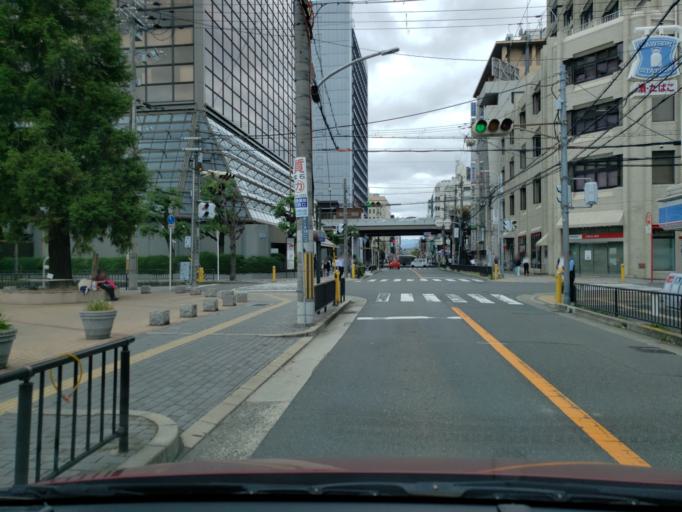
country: JP
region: Osaka
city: Suita
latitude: 34.7598
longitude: 135.4985
